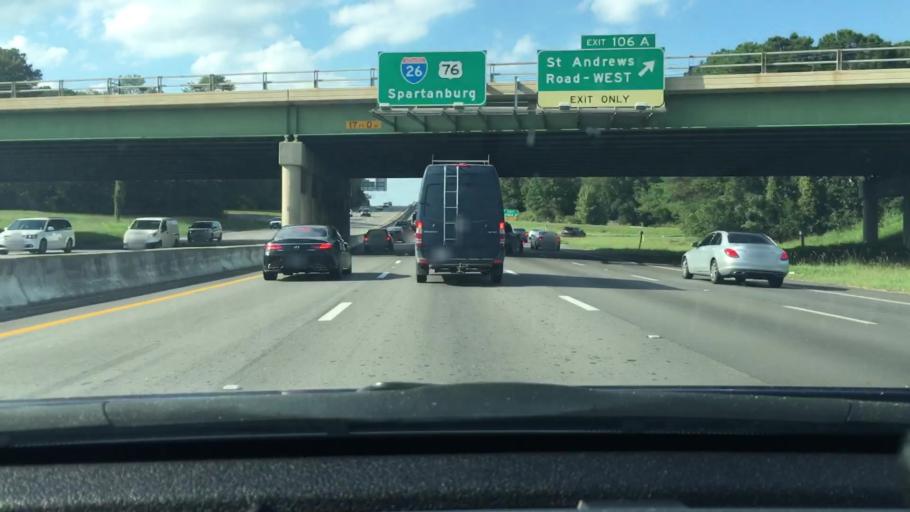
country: US
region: South Carolina
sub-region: Lexington County
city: Saint Andrews
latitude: 34.0443
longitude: -81.1177
